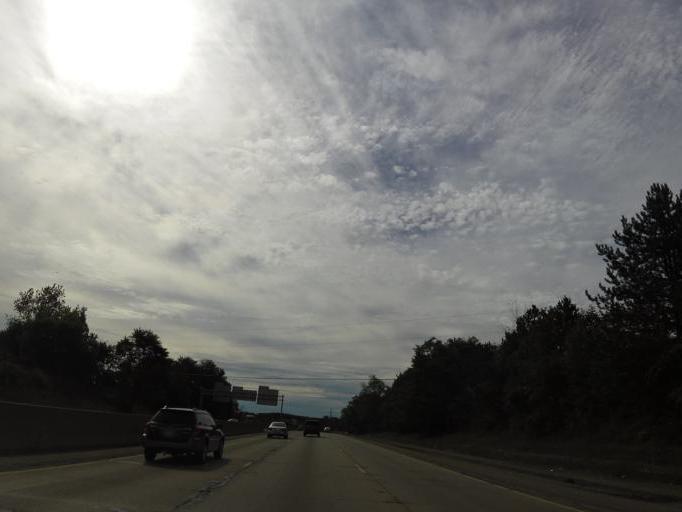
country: US
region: Ohio
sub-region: Summit County
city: Boston Heights
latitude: 41.2232
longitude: -81.4895
